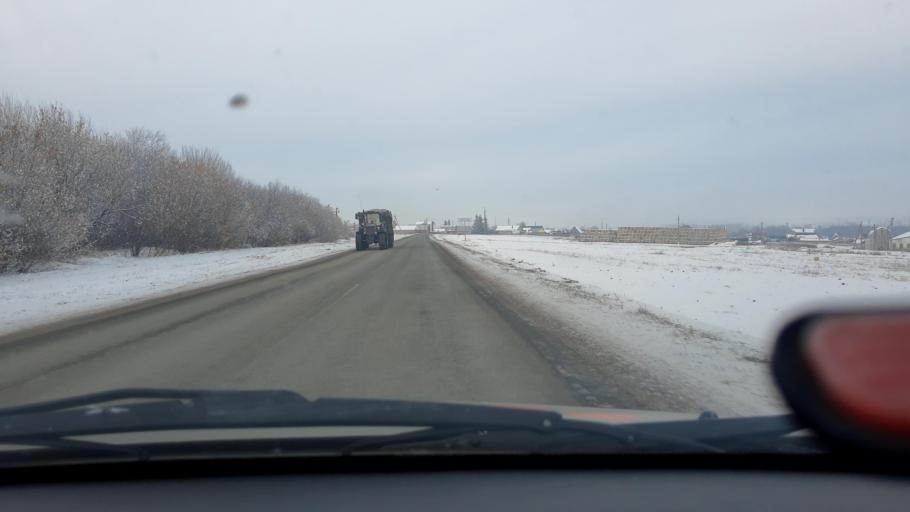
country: RU
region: Bashkortostan
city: Avdon
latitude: 54.4075
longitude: 55.8055
